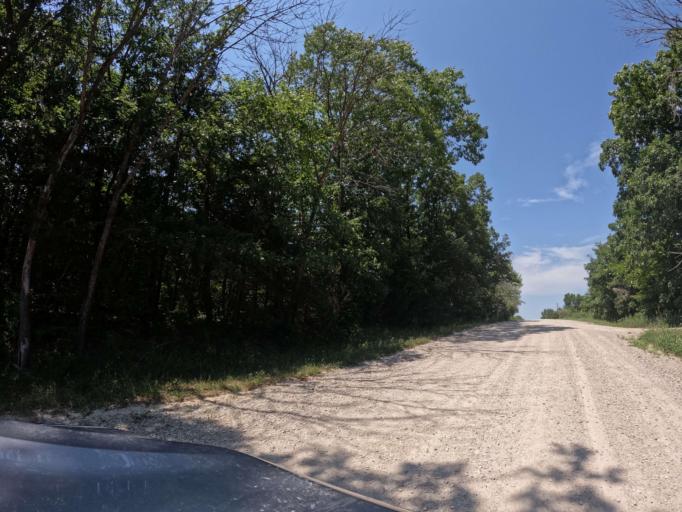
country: US
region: Iowa
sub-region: Henry County
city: Mount Pleasant
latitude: 40.8920
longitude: -91.6891
